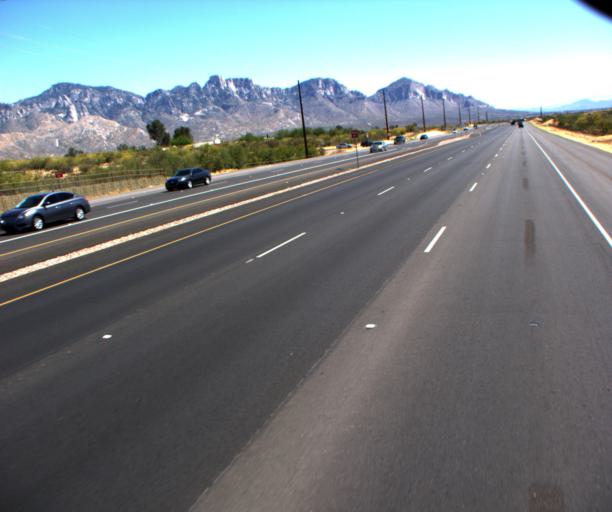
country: US
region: Arizona
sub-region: Pima County
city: Catalina
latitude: 32.4664
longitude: -110.9260
